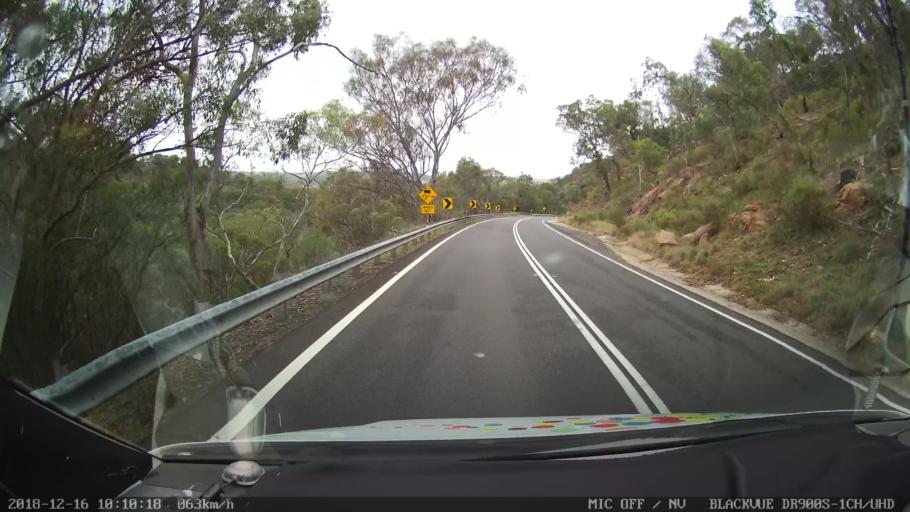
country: AU
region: New South Wales
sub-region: Glen Innes Severn
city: Glen Innes
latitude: -29.3189
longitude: 151.9230
